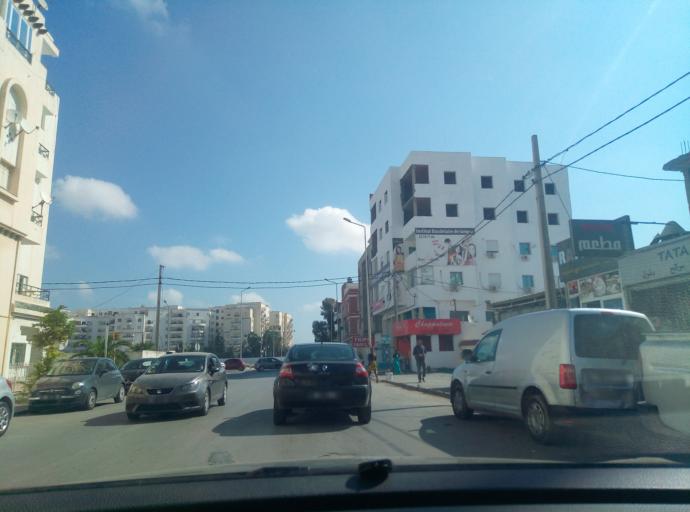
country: TN
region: Tunis
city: La Goulette
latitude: 36.8591
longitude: 10.2703
